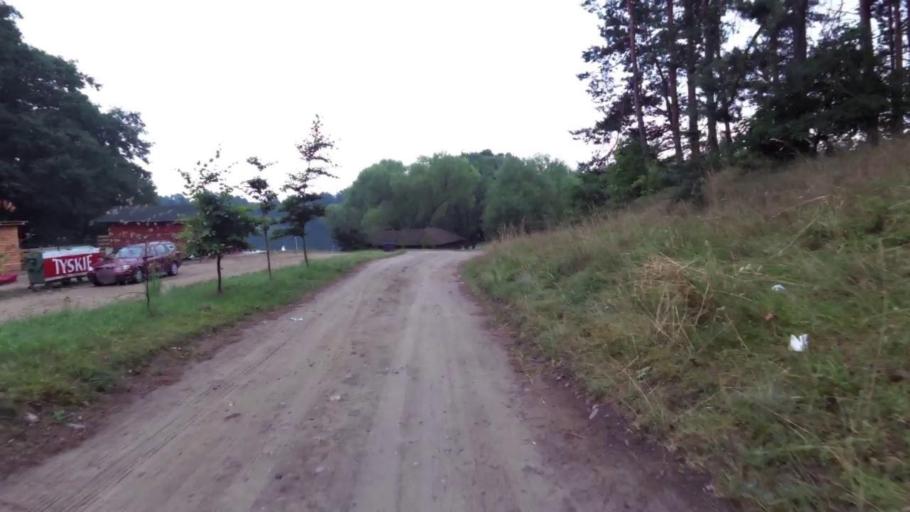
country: PL
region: West Pomeranian Voivodeship
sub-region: Powiat szczecinecki
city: Lubowo
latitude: 53.5920
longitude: 16.3892
